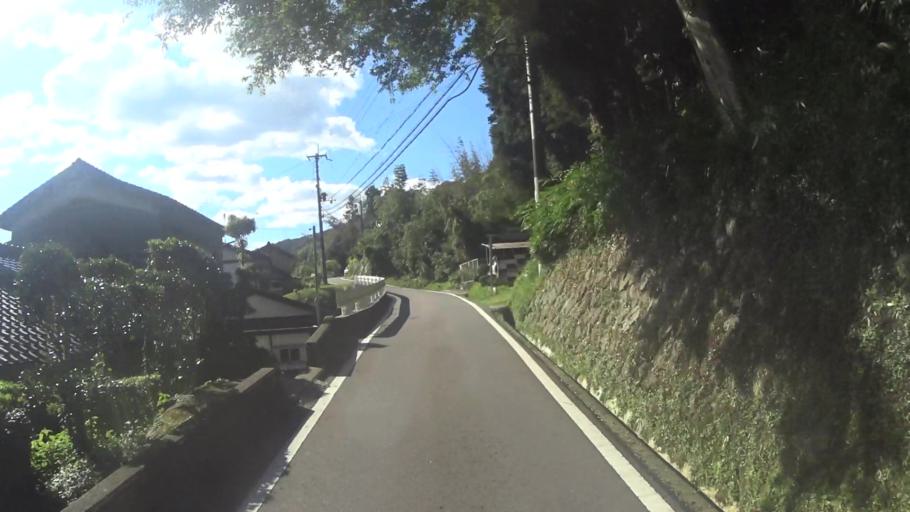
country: JP
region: Nara
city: Nara-shi
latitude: 34.7659
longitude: 135.9126
